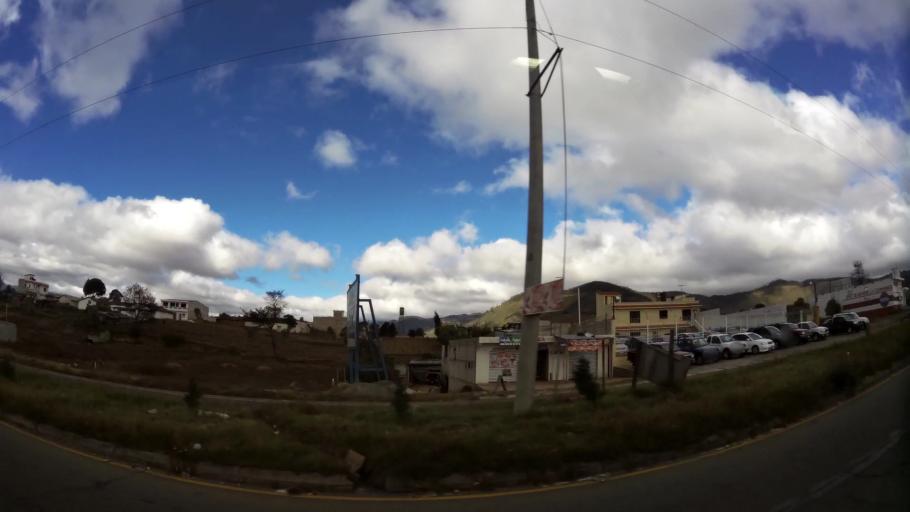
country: GT
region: Quetzaltenango
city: Salcaja
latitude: 14.8798
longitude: -91.4697
